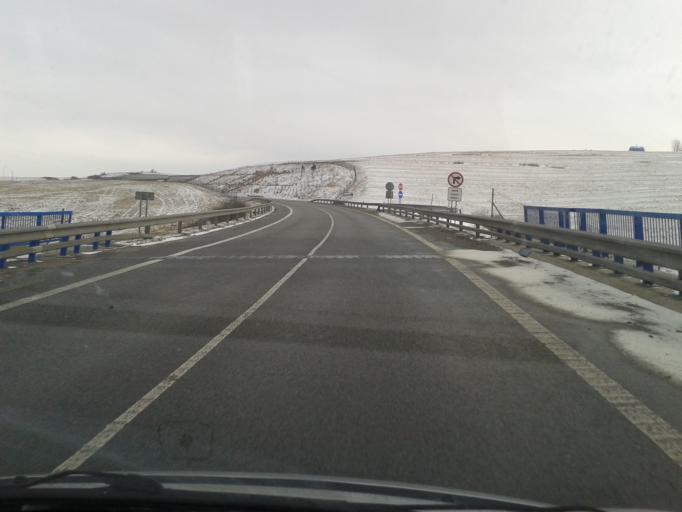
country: SK
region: Zilinsky
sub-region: Okres Zilina
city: Trstena
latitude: 49.3528
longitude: 19.6176
